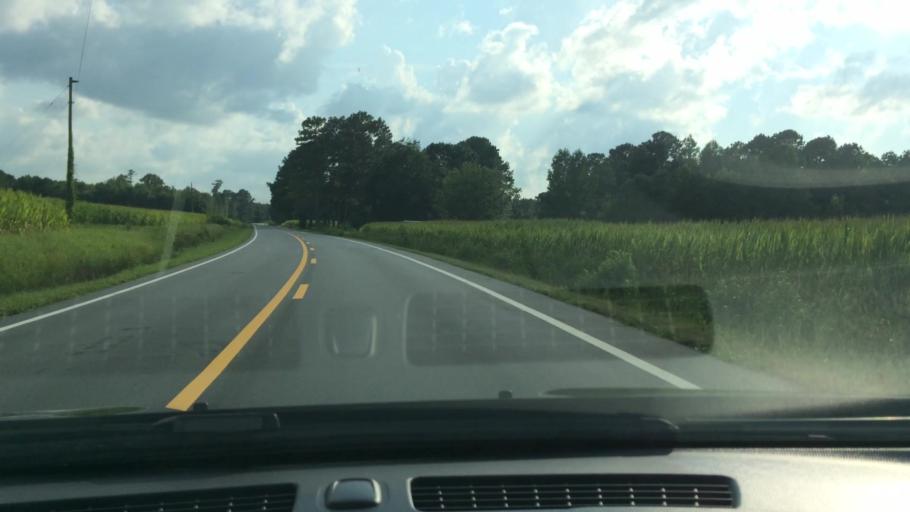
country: US
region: North Carolina
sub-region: Craven County
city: Vanceboro
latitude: 35.4345
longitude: -77.1697
